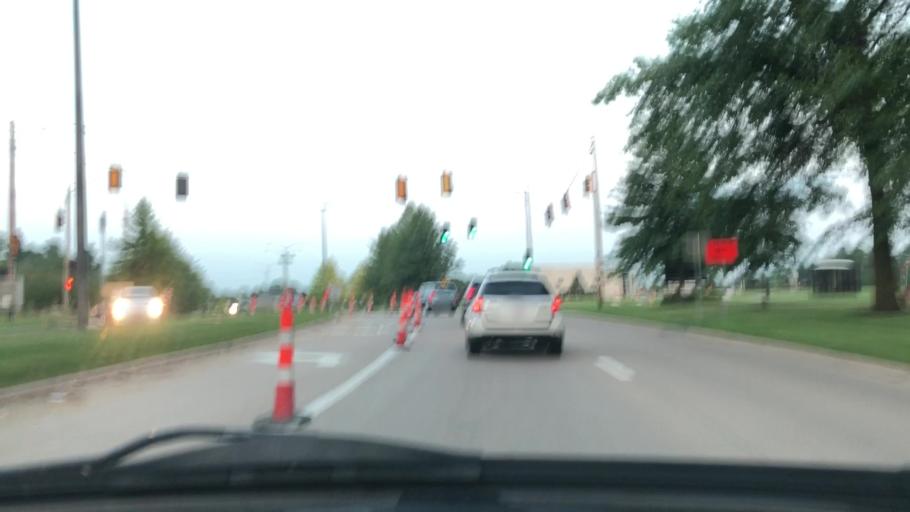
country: US
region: Iowa
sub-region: Johnson County
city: Coralville
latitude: 41.7084
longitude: -91.6056
